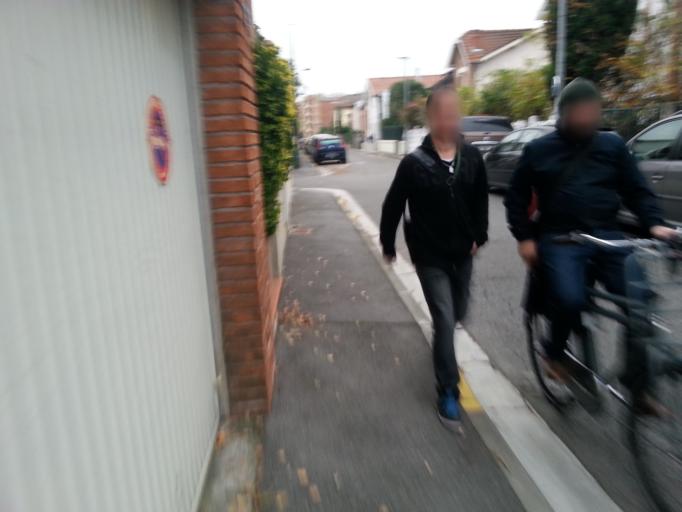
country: FR
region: Midi-Pyrenees
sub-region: Departement de la Haute-Garonne
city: Toulouse
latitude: 43.5988
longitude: 1.4667
